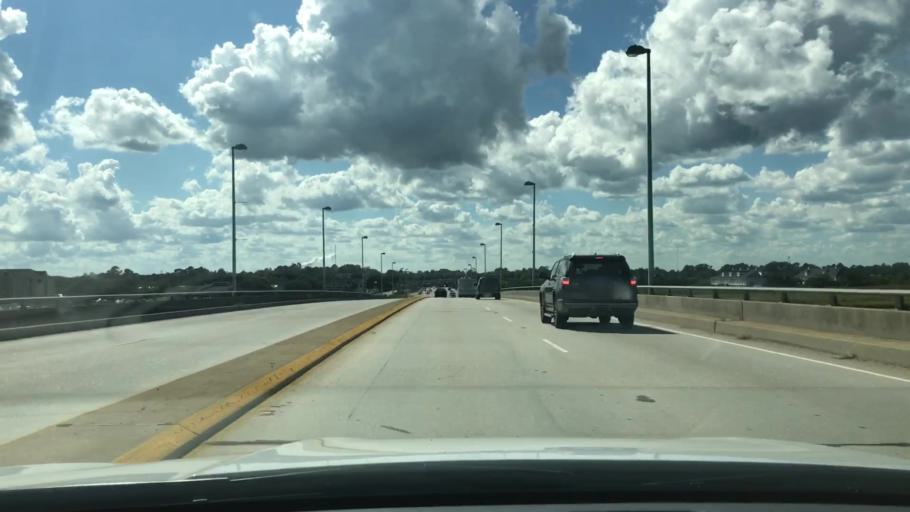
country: US
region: South Carolina
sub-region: Georgetown County
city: Georgetown
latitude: 33.3664
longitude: -79.2648
